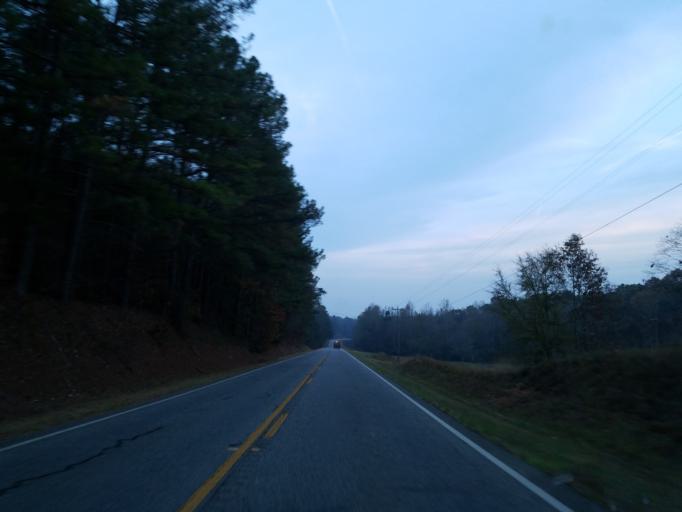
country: US
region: Georgia
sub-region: Gilmer County
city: Ellijay
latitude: 34.5736
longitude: -84.6141
